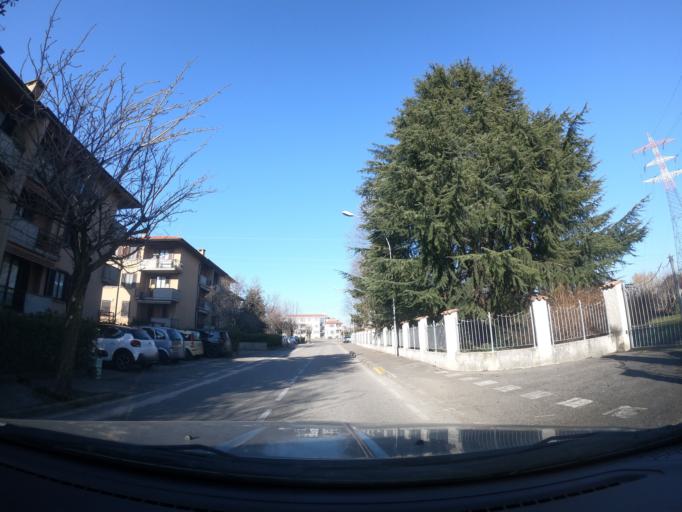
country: IT
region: Lombardy
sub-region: Provincia di Monza e Brianza
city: Sulbiate
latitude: 45.6363
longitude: 9.4294
